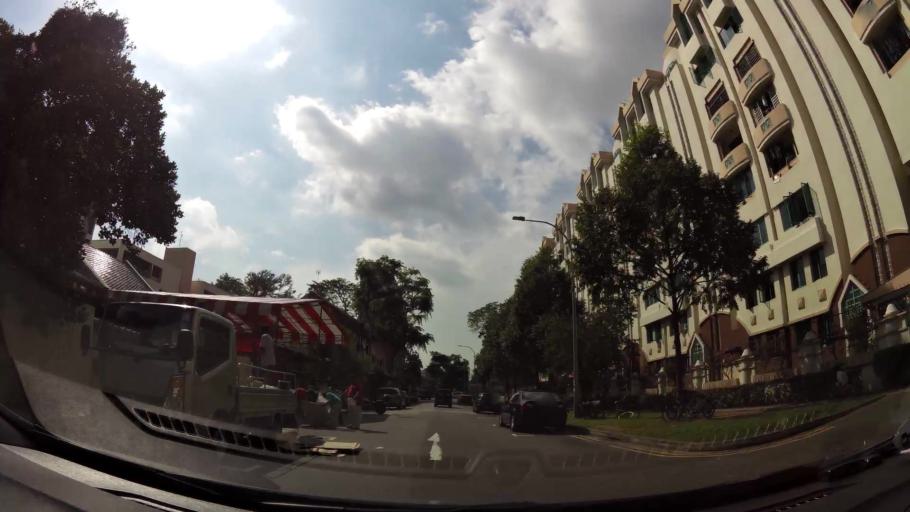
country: SG
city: Singapore
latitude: 1.3109
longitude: 103.8792
